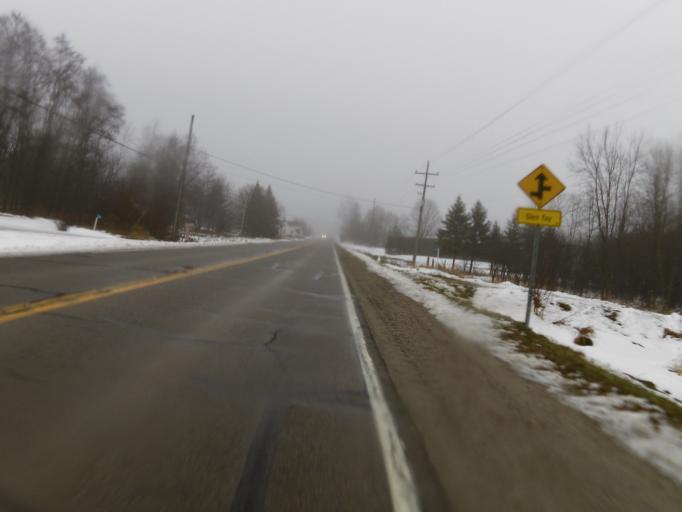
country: CA
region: Ontario
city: Perth
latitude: 44.8814
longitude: -76.3108
